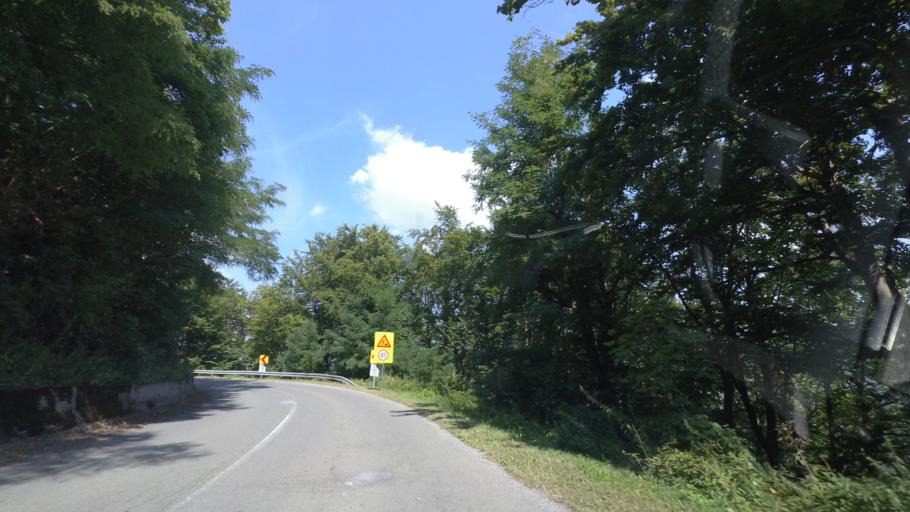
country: BA
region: Federation of Bosnia and Herzegovina
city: Zboriste
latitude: 45.1549
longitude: 16.1495
